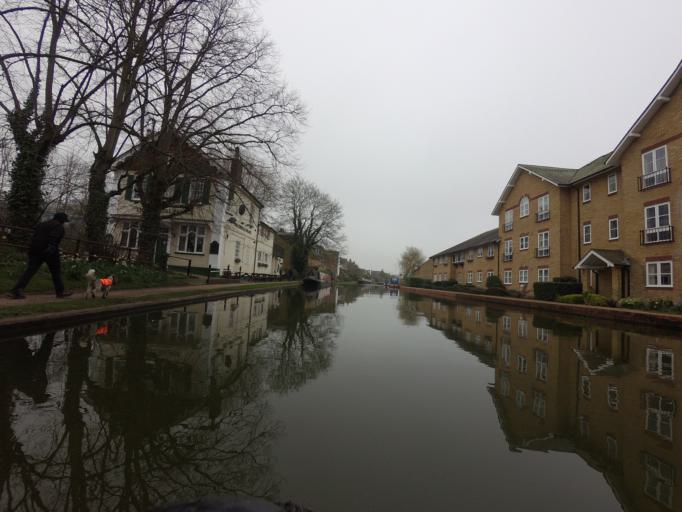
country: GB
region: England
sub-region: Hertfordshire
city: Berkhamsted
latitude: 51.7622
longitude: -0.5595
